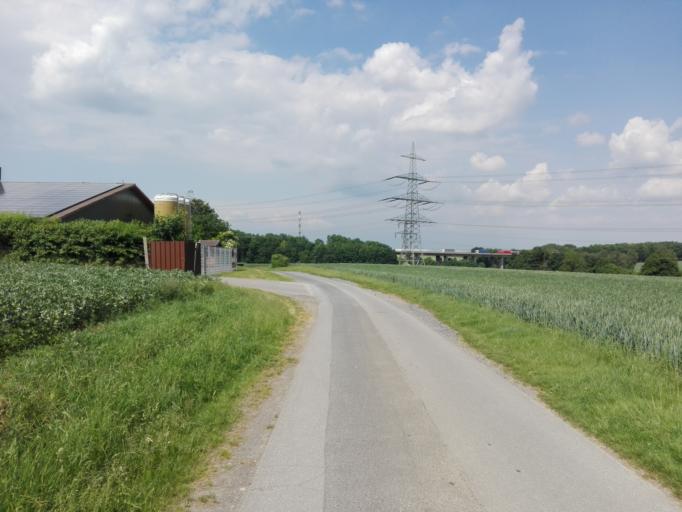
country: DE
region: North Rhine-Westphalia
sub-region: Regierungsbezirk Arnsberg
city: Unna
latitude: 51.5235
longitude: 7.7267
